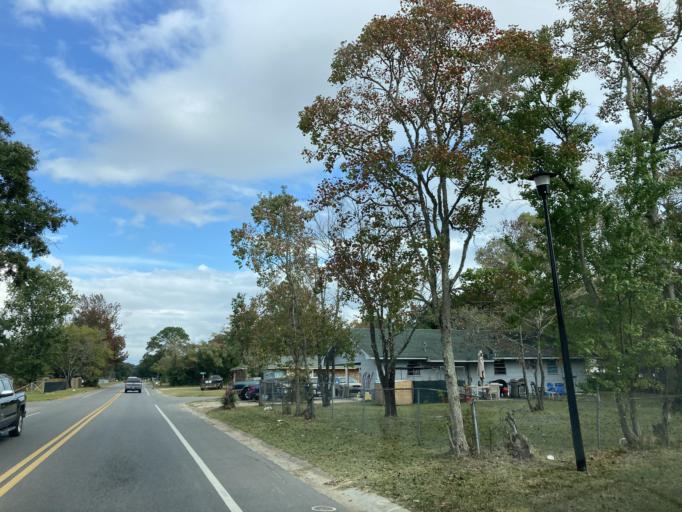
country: US
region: Mississippi
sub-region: Jackson County
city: Gulf Hills
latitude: 30.4360
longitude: -88.8271
